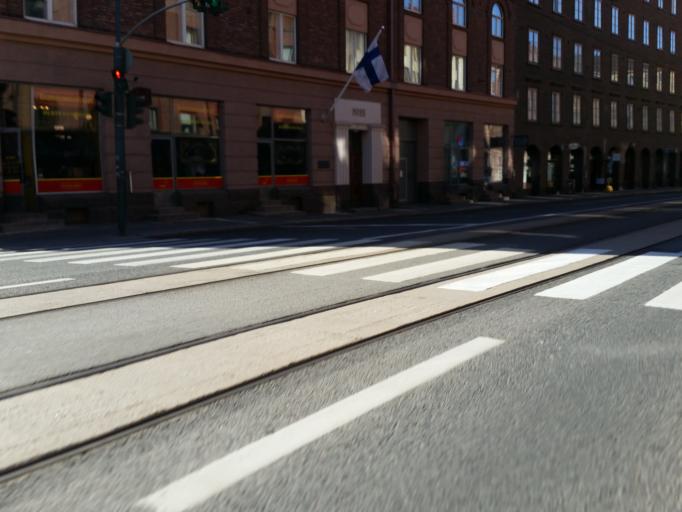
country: FI
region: Uusimaa
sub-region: Helsinki
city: Helsinki
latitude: 60.1741
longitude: 24.9224
